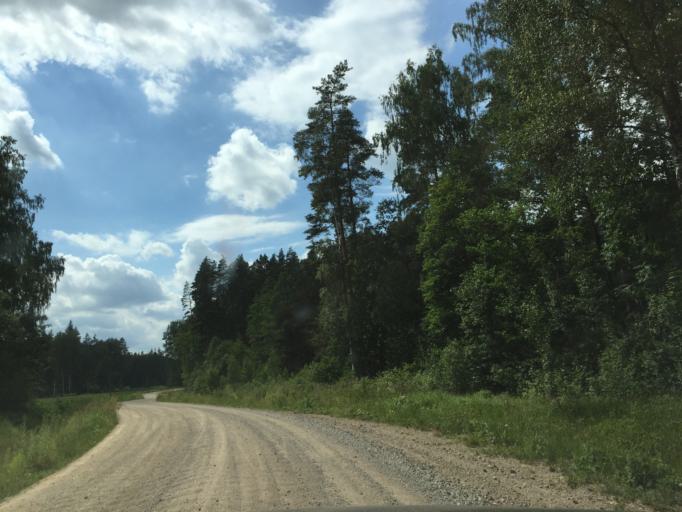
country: LV
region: Jelgava
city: Jelgava
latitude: 56.6268
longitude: 23.6593
